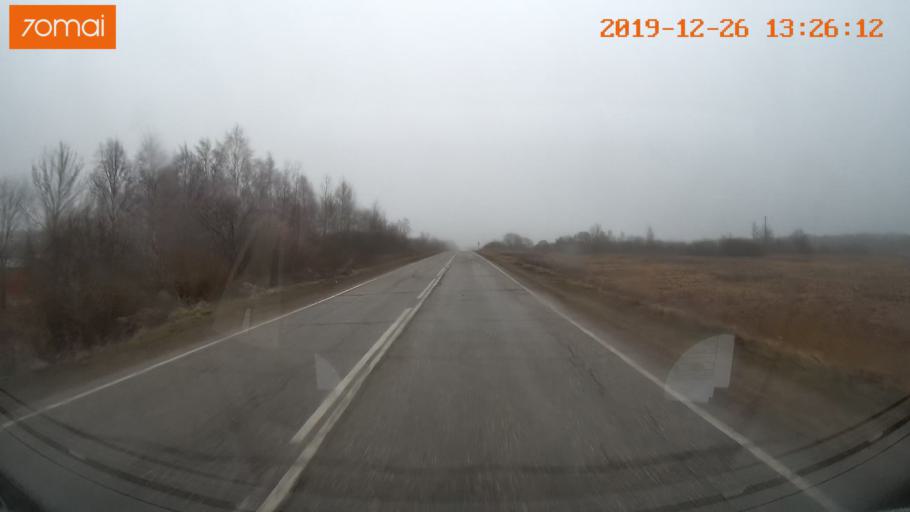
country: RU
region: Vologda
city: Cherepovets
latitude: 58.8671
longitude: 38.2218
